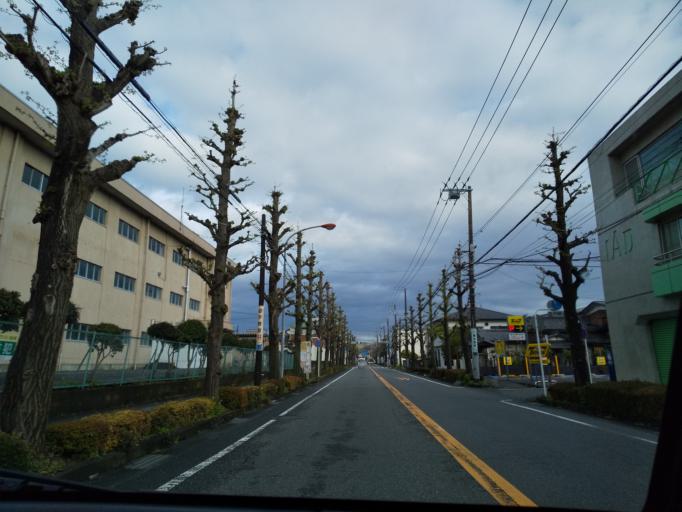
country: JP
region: Tokyo
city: Hachioji
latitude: 35.5992
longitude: 139.3437
